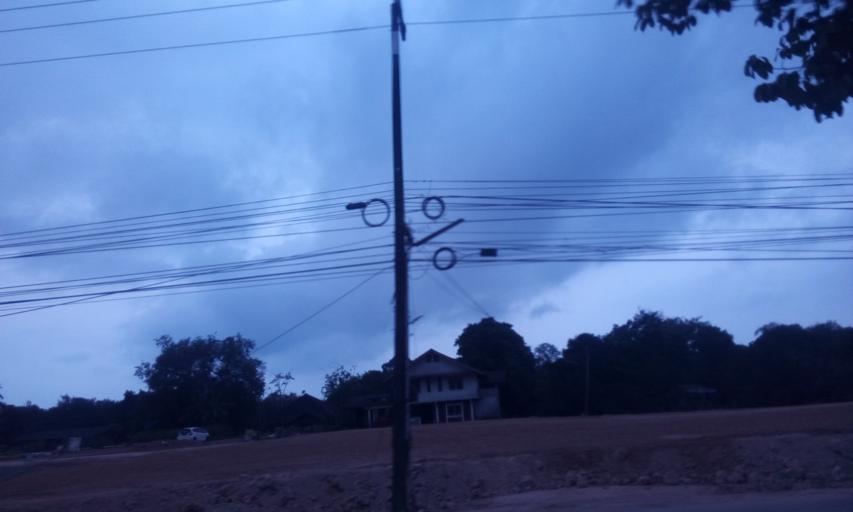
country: TH
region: Chanthaburi
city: Khlung
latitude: 12.4568
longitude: 102.2354
